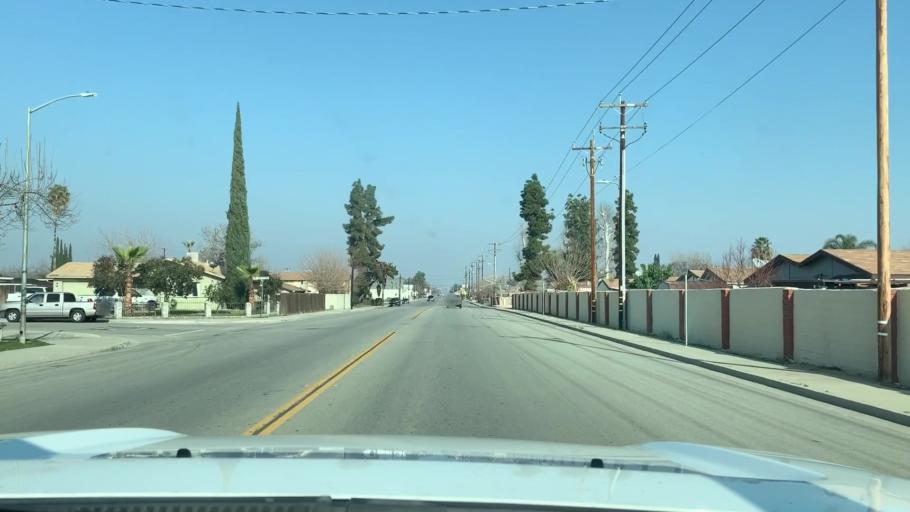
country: US
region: California
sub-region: Kern County
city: Shafter
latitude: 35.4941
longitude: -119.2784
